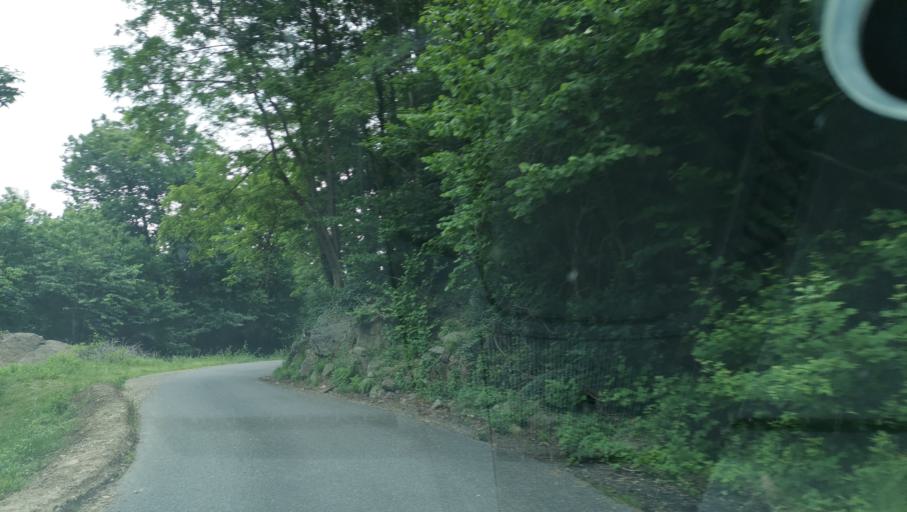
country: IT
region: Piedmont
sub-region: Provincia di Torino
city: Quassolo
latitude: 45.5236
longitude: 7.8294
